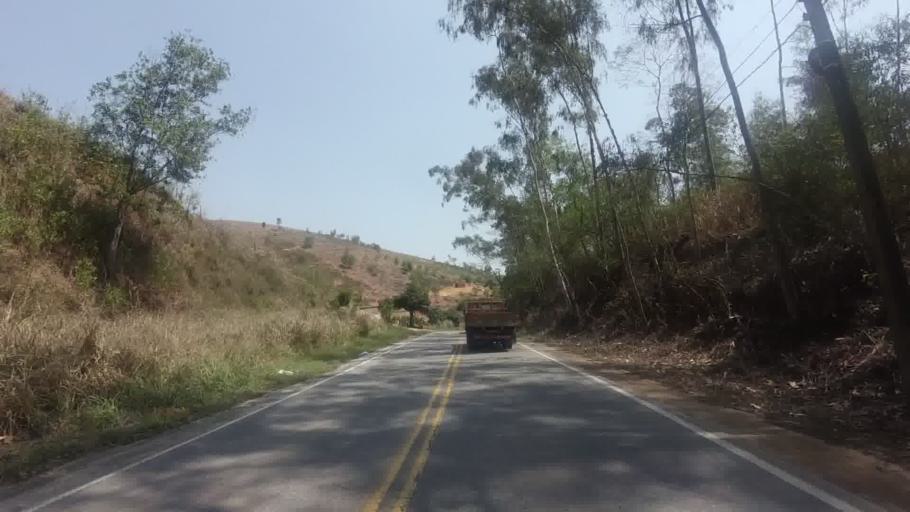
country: BR
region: Espirito Santo
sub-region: Rio Novo Do Sul
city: Rio Novo do Sul
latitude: -20.8775
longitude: -41.0136
